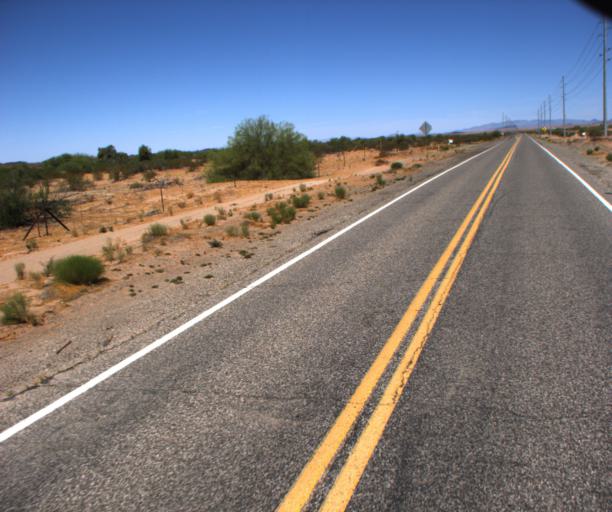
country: US
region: Arizona
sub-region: La Paz County
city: Cienega Springs
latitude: 33.9578
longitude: -114.0286
